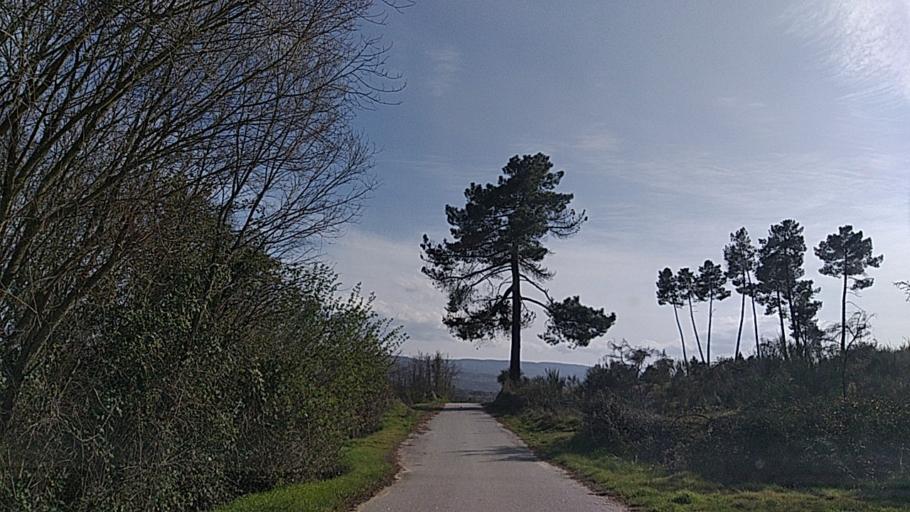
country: PT
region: Guarda
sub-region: Celorico da Beira
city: Celorico da Beira
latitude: 40.6459
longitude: -7.4285
